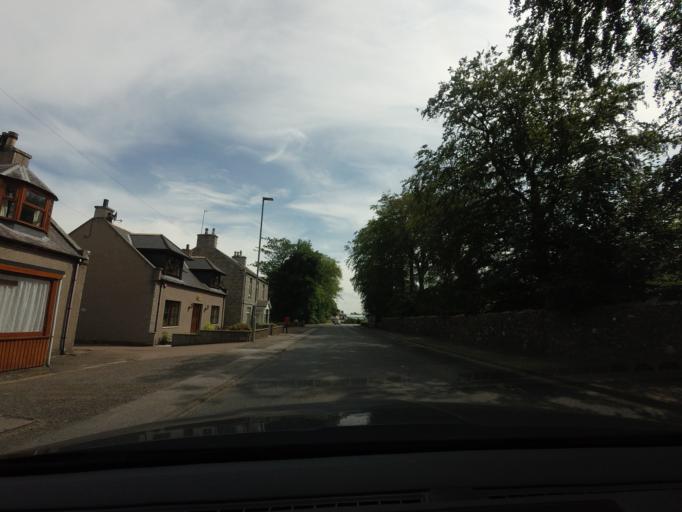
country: GB
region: Scotland
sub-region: Aberdeenshire
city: Mintlaw
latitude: 57.5260
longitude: -2.0211
